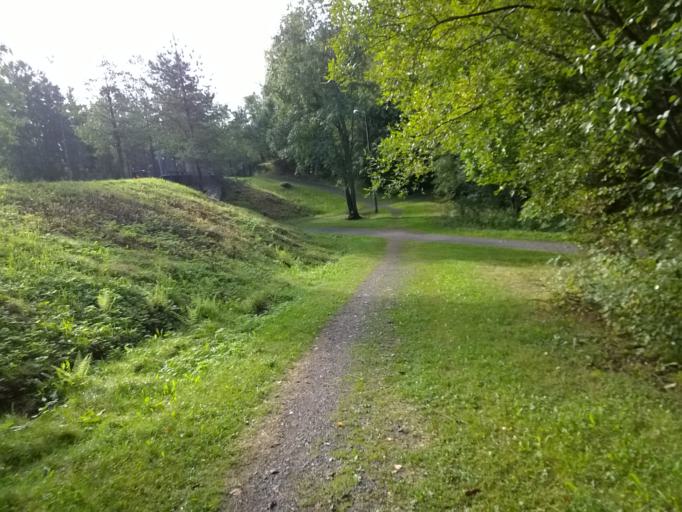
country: FI
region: Pirkanmaa
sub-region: Tampere
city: Tampere
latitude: 61.4422
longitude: 23.8422
